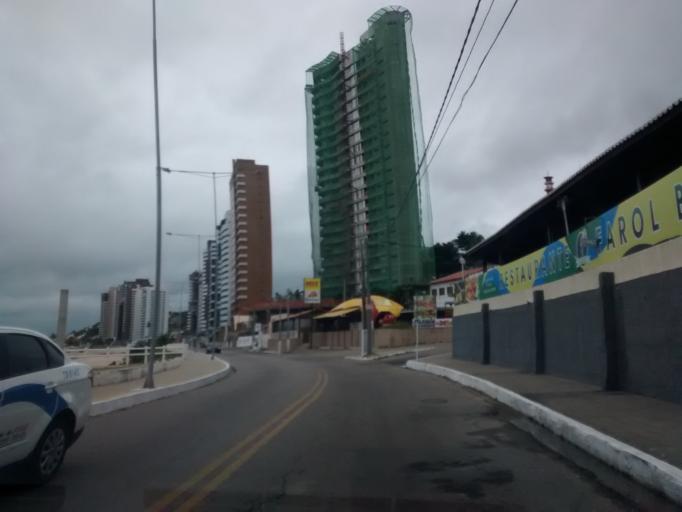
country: BR
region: Rio Grande do Norte
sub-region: Natal
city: Natal
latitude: -5.7856
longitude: -35.1903
